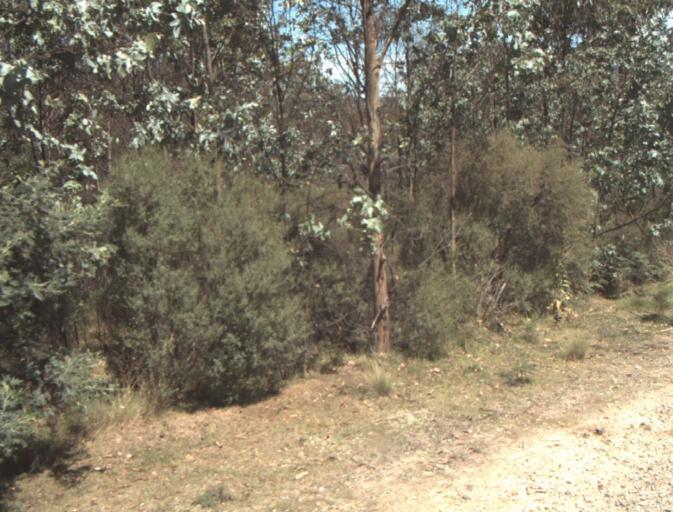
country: AU
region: Tasmania
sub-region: Dorset
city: Scottsdale
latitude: -41.3130
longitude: 147.4656
